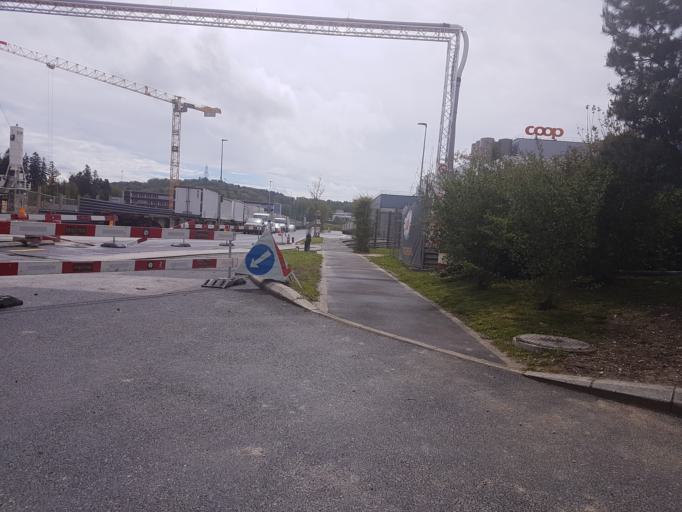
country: CH
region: Vaud
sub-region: Ouest Lausannois District
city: Bussigny
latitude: 46.5675
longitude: 6.5260
